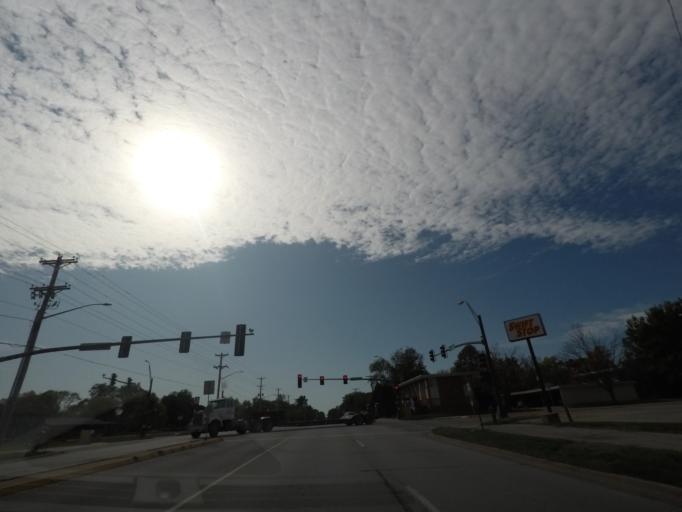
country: US
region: Iowa
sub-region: Story County
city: Ames
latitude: 42.0466
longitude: -93.6207
